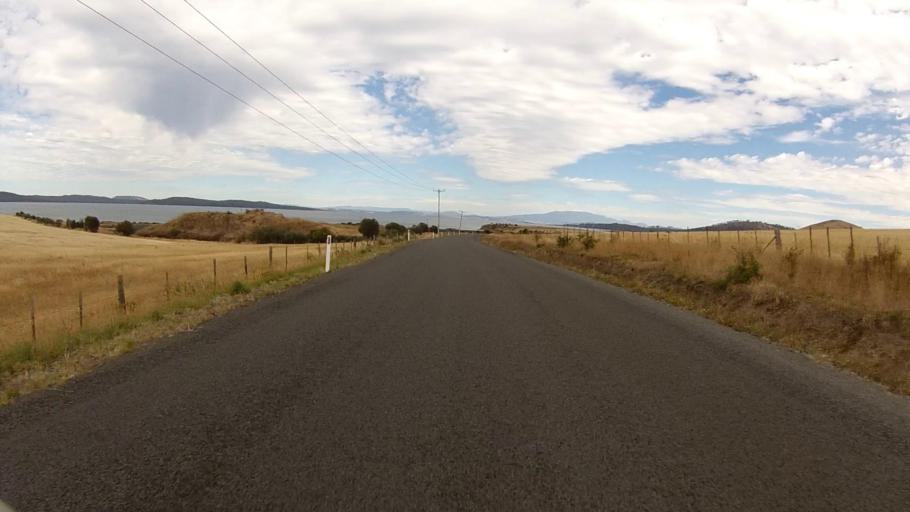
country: AU
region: Tasmania
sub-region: Sorell
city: Sorell
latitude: -42.8995
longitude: 147.7653
